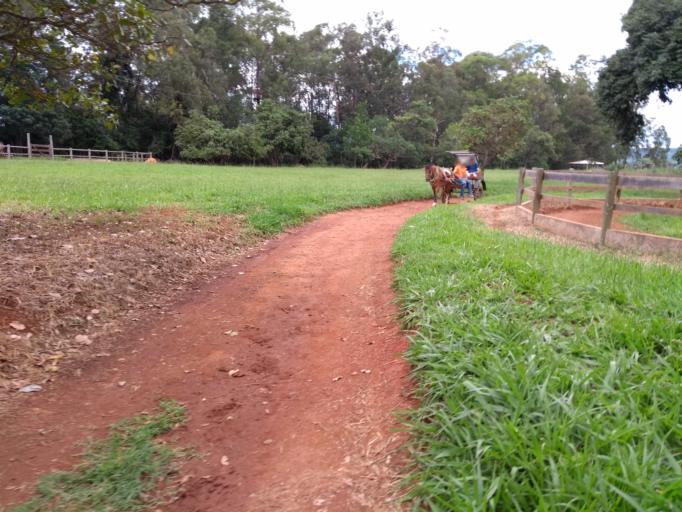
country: BR
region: Federal District
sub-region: Brasilia
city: Brasilia
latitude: -15.6611
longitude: -47.7721
